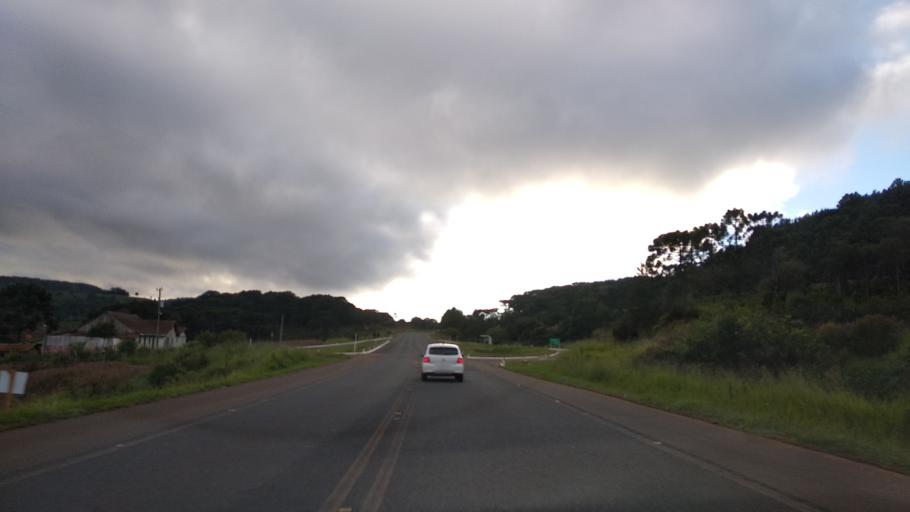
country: BR
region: Santa Catarina
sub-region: Curitibanos
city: Curitibanos
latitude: -27.5790
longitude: -50.7725
